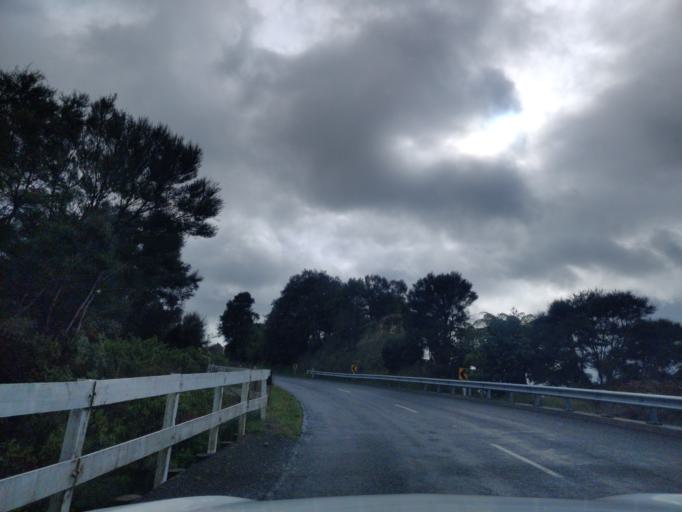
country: NZ
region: Manawatu-Wanganui
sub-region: Palmerston North City
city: Palmerston North
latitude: -40.1937
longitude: 175.7822
